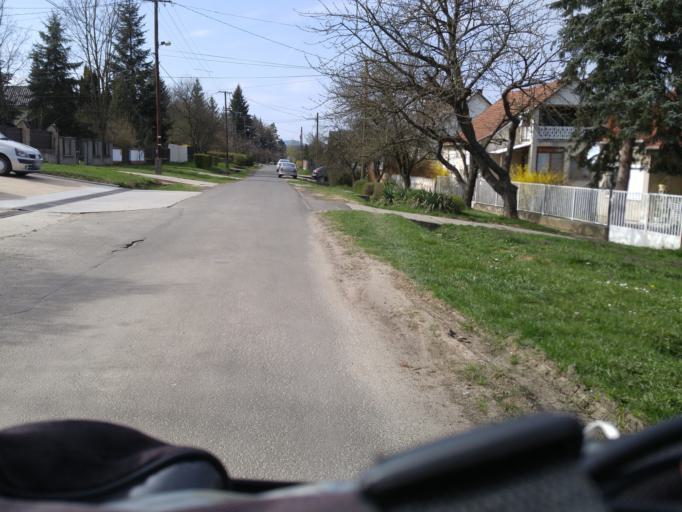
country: HU
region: Nograd
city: Retsag
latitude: 47.9231
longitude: 19.1721
